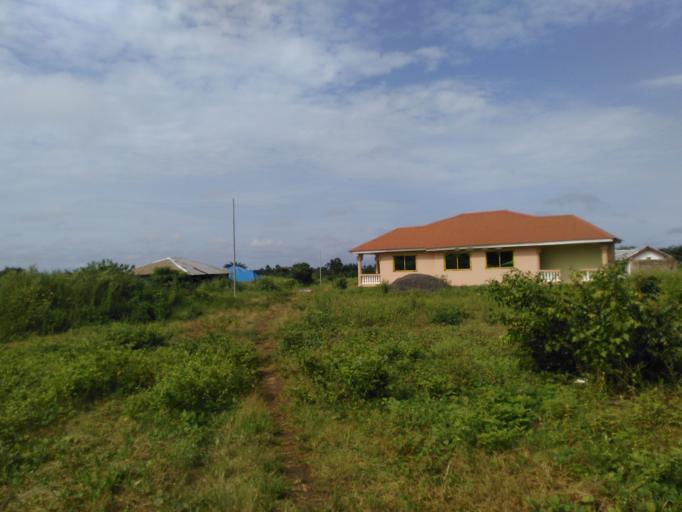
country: SL
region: Southern Province
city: Rotifunk
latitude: 8.4854
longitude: -12.7598
